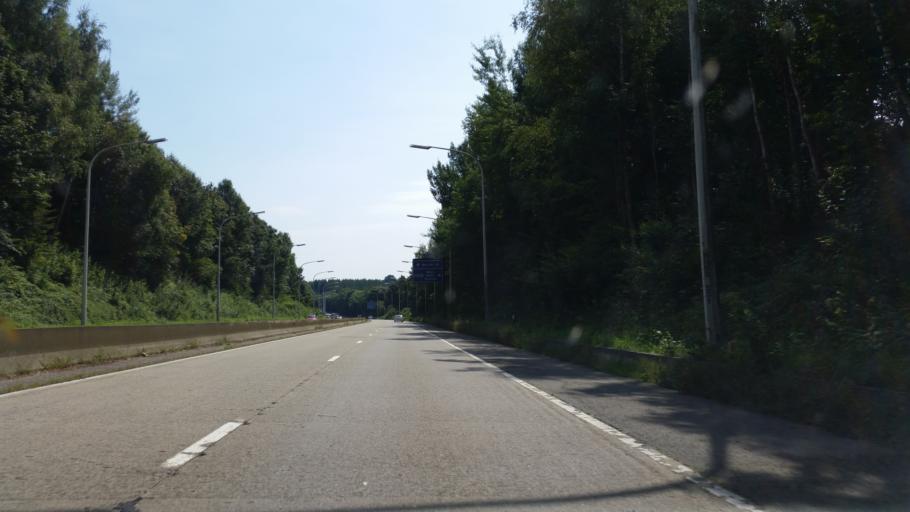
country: BE
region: Wallonia
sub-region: Province de Namur
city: Hamois
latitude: 50.2921
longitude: 5.1748
